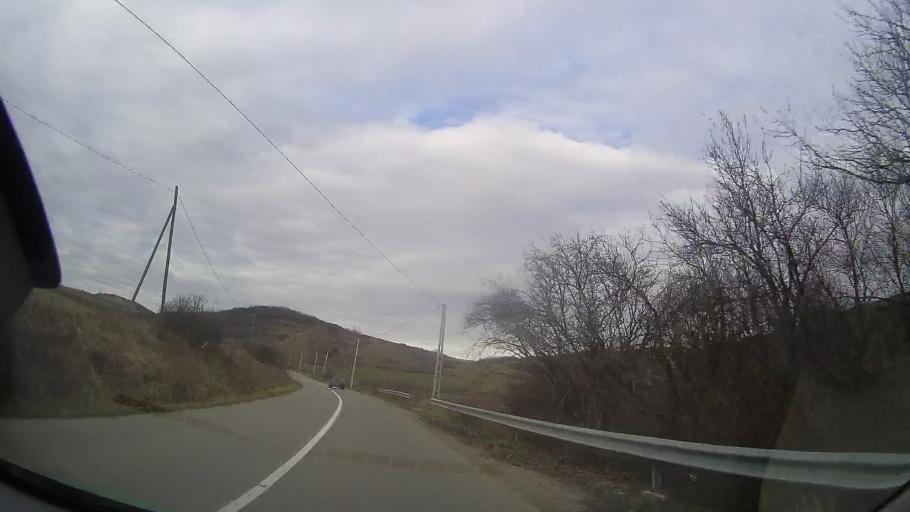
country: RO
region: Bistrita-Nasaud
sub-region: Comuna Milas
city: Milas
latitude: 46.8366
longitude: 24.4482
